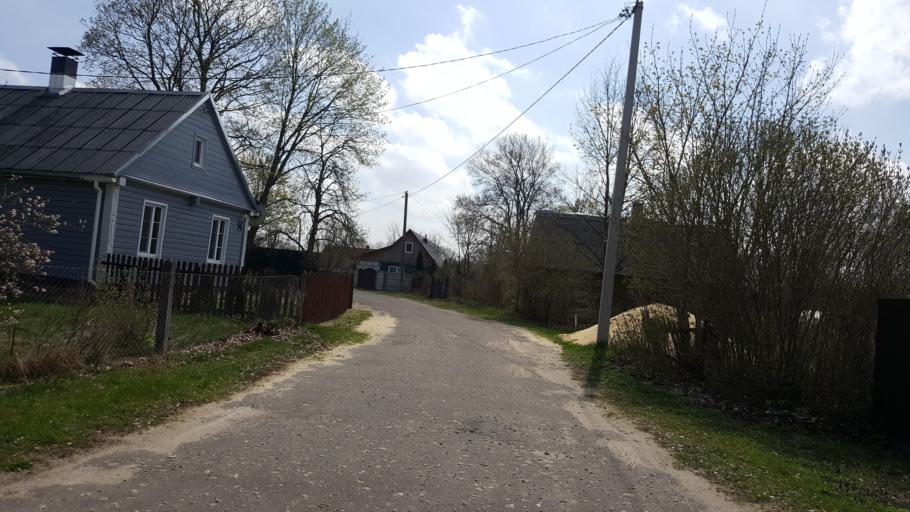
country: BY
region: Brest
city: Zhabinka
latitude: 52.2541
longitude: 23.9642
